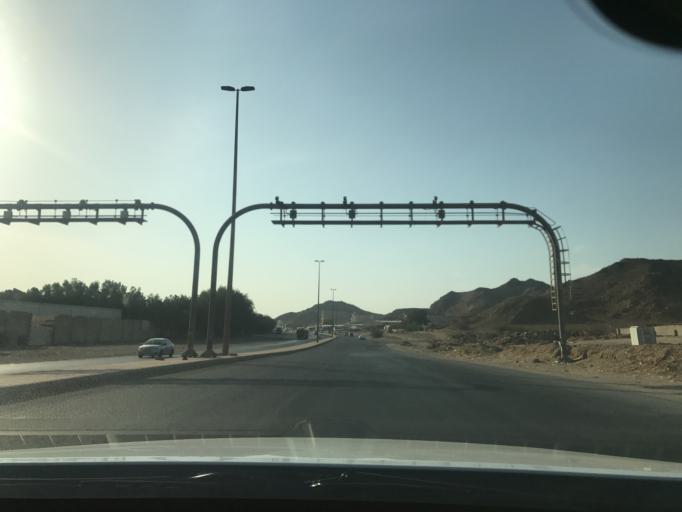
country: SA
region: Makkah
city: Jeddah
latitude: 21.4065
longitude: 39.4277
